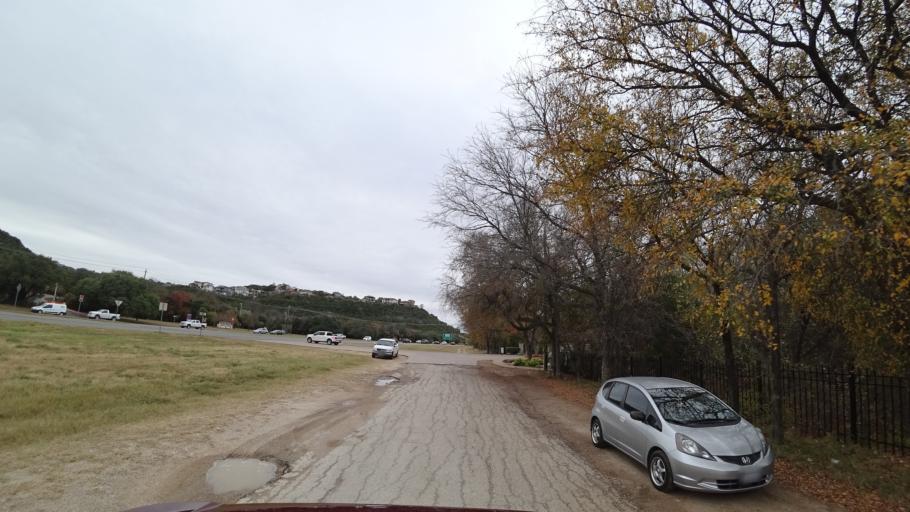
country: US
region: Texas
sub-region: Williamson County
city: Jollyville
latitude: 30.3768
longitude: -97.7805
